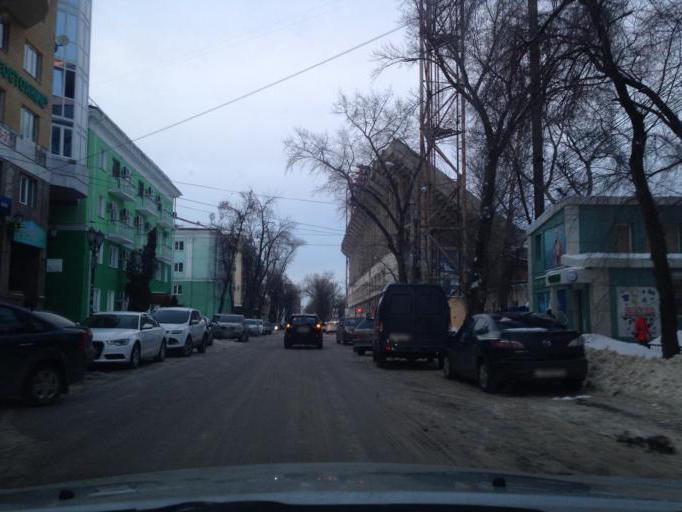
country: RU
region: Voronezj
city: Voronezh
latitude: 51.6718
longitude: 39.2019
